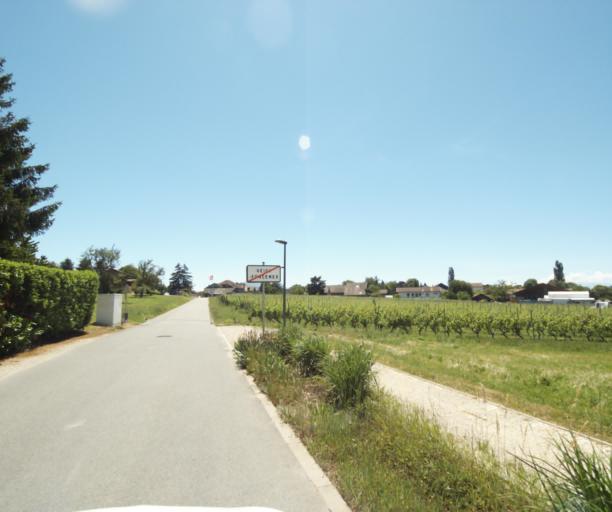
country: FR
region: Rhone-Alpes
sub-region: Departement de la Haute-Savoie
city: Veigy-Foncenex
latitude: 46.2548
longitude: 6.2617
